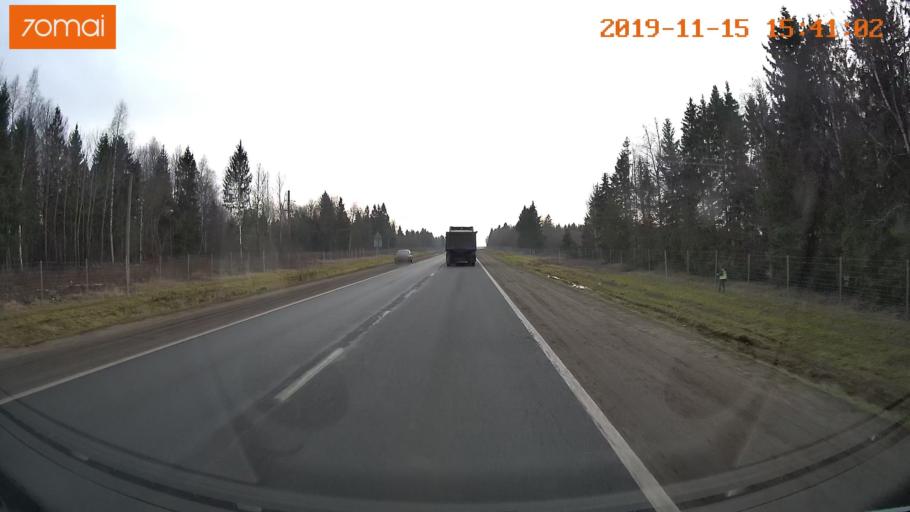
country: RU
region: Jaroslavl
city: Danilov
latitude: 58.0051
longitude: 40.0514
